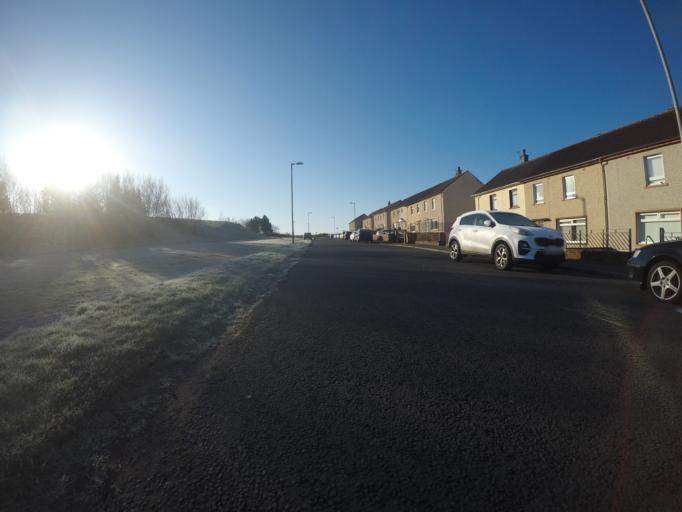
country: GB
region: Scotland
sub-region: North Ayrshire
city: Stevenston
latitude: 55.6310
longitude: -4.7400
